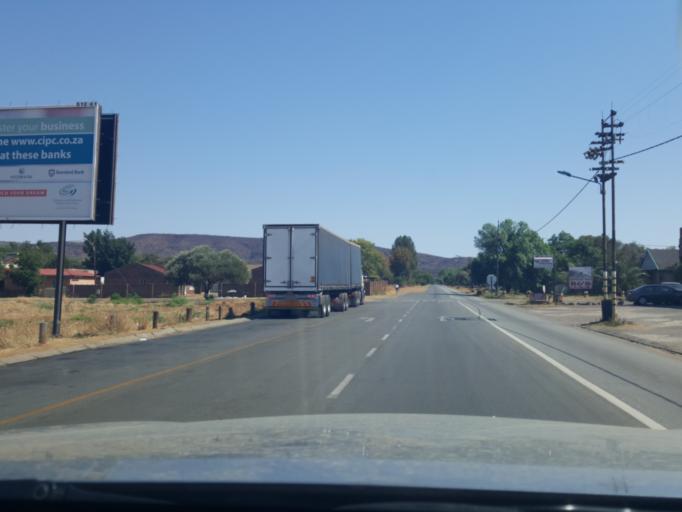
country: ZA
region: North-West
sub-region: Ngaka Modiri Molema District Municipality
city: Zeerust
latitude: -25.5330
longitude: 26.0763
